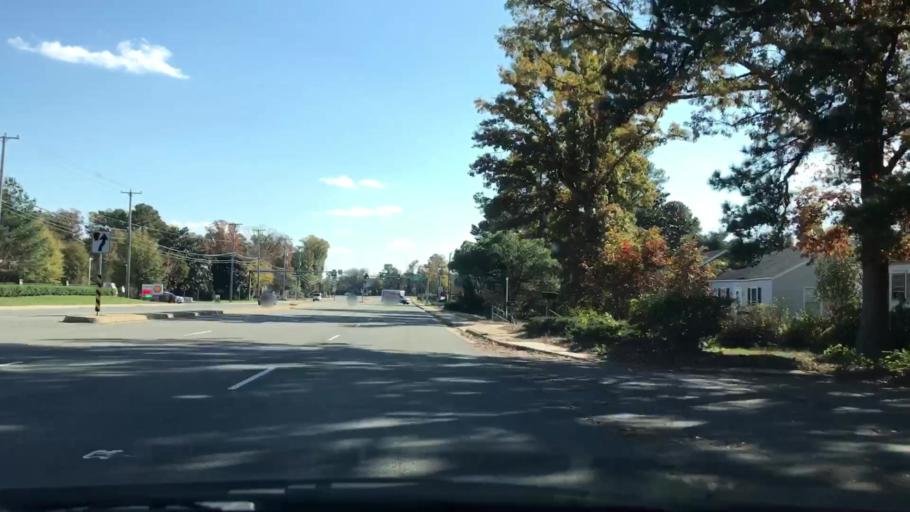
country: US
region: Virginia
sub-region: Henrico County
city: Dumbarton
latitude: 37.6087
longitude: -77.4959
